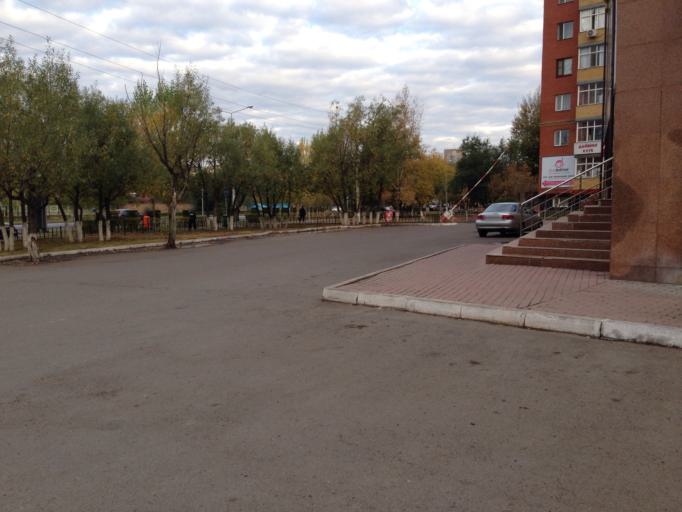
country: KZ
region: Astana Qalasy
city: Astana
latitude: 51.1470
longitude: 71.4599
